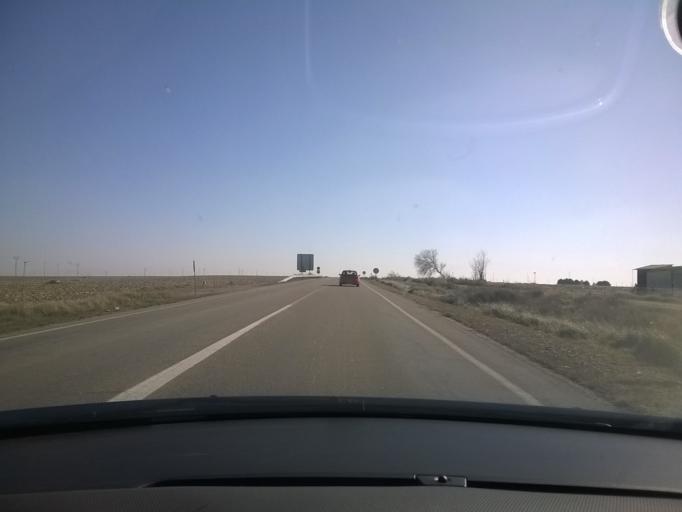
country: ES
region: Aragon
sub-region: Provincia de Zaragoza
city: Bujaraloz
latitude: 41.5183
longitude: -0.1746
